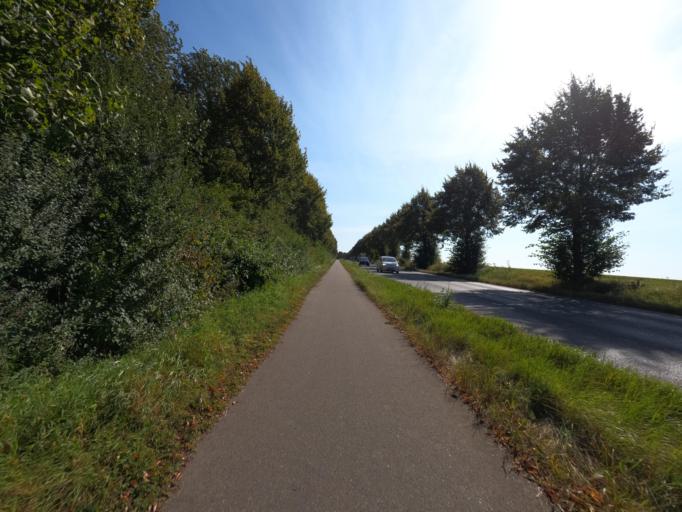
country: DE
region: North Rhine-Westphalia
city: Siersdorf
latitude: 50.9071
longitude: 6.2188
